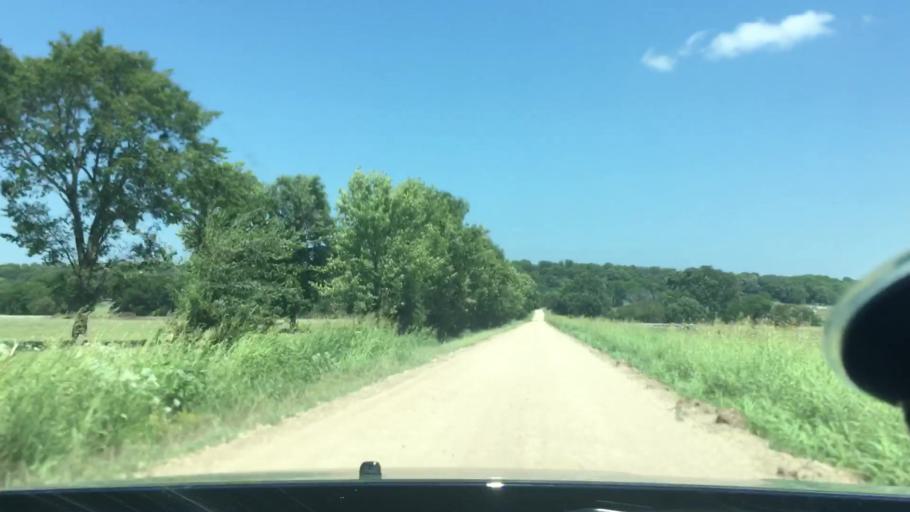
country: US
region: Oklahoma
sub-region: Johnston County
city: Tishomingo
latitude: 34.3581
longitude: -96.4420
